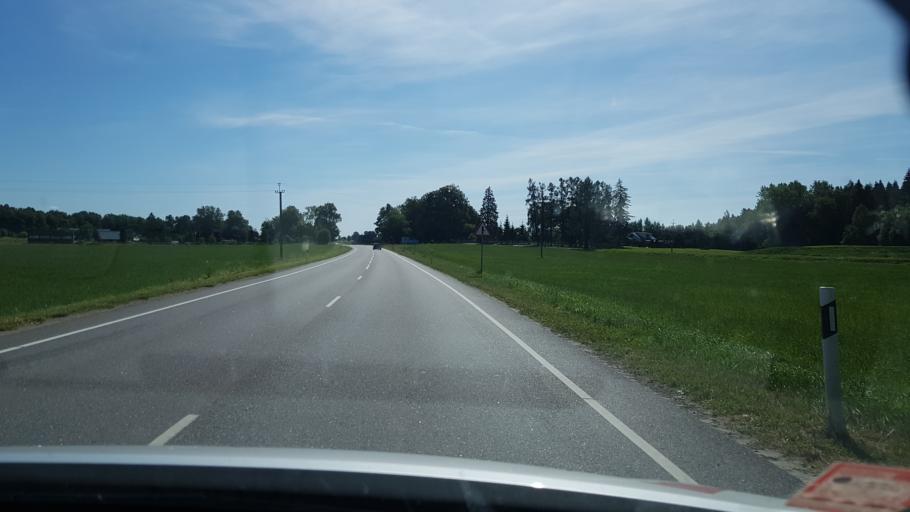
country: EE
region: Tartu
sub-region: Tartu linn
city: Tartu
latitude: 58.4362
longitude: 26.8305
